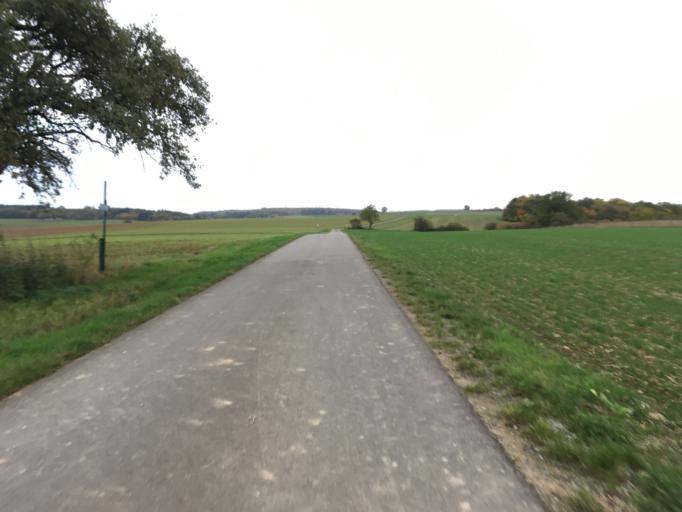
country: DE
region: Baden-Wuerttemberg
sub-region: Karlsruhe Region
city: Seckach
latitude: 49.4683
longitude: 9.3759
